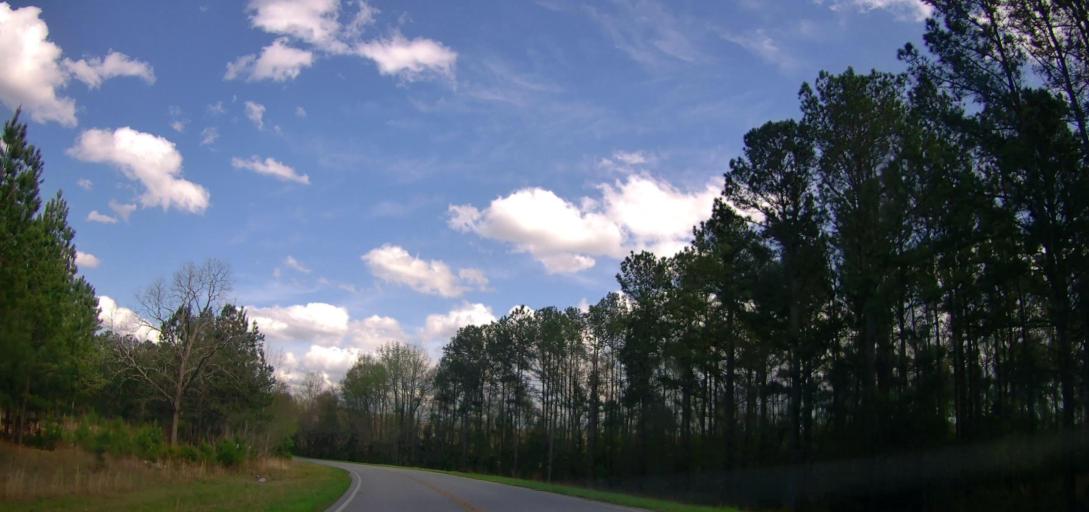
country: US
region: Georgia
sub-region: Wilkinson County
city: Gordon
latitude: 32.8260
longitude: -83.4227
